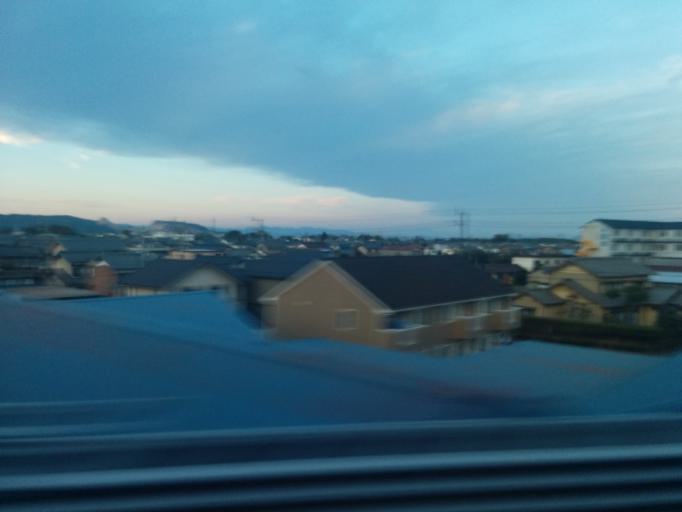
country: JP
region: Gifu
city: Tarui
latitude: 35.3557
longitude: 136.5446
